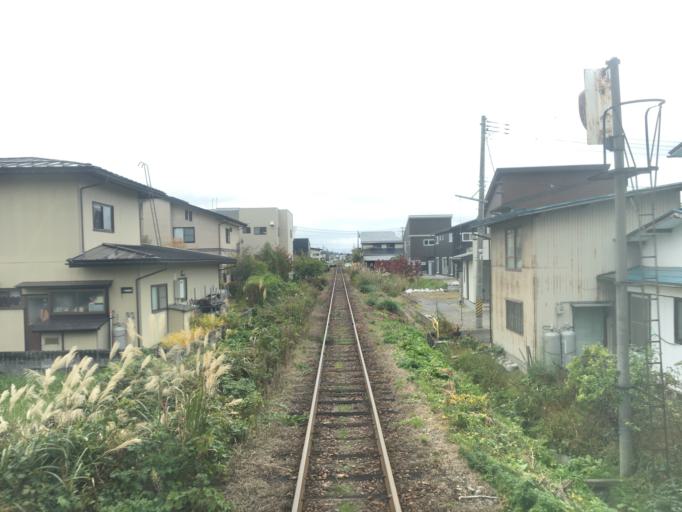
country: JP
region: Yamagata
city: Nagai
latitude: 38.1000
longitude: 140.0344
